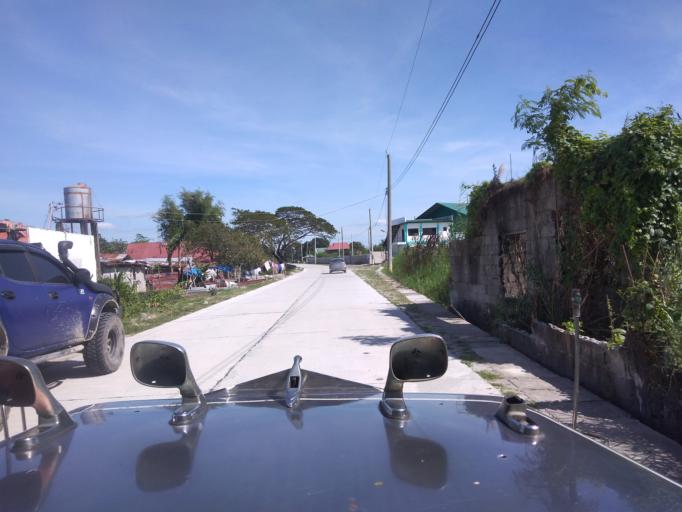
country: PH
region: Central Luzon
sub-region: Province of Pampanga
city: Magliman
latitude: 15.0267
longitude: 120.6616
